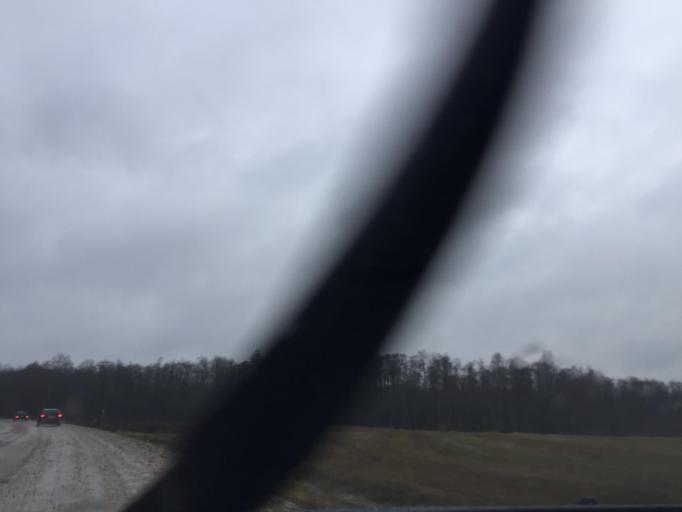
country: LV
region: Salacgrivas
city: Salacgriva
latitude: 57.7720
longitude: 24.5245
